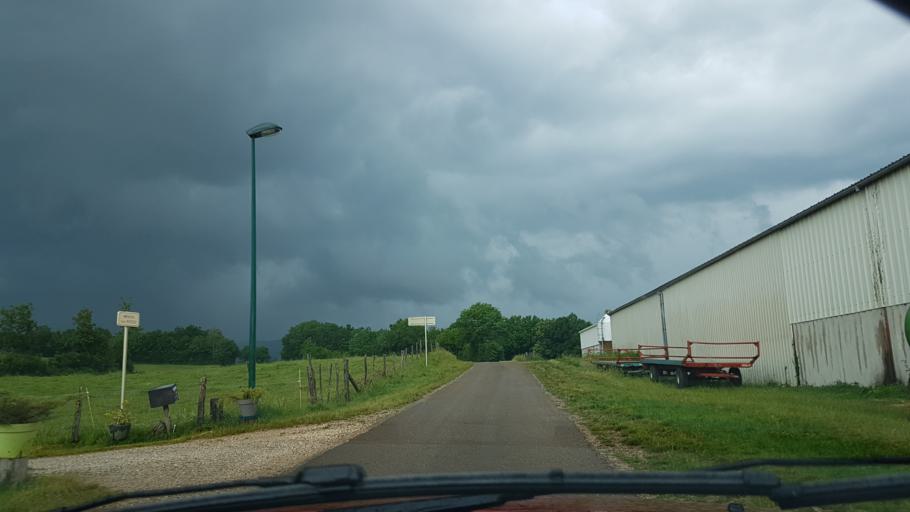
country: FR
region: Franche-Comte
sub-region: Departement du Jura
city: Clairvaux-les-Lacs
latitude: 46.5318
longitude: 5.7131
